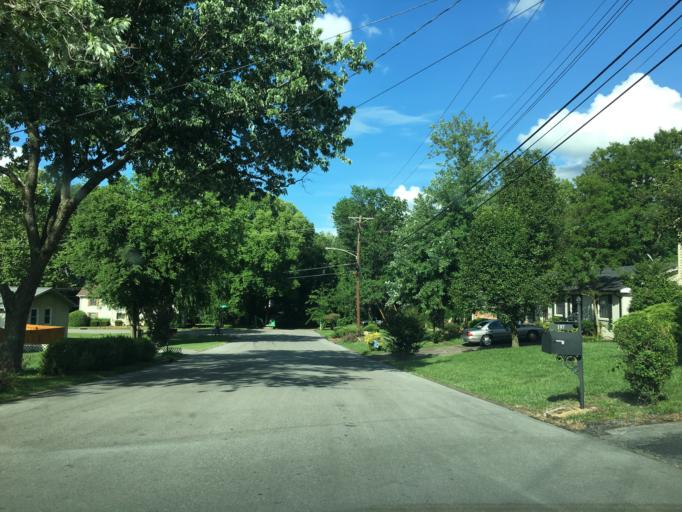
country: US
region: Tennessee
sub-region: Davidson County
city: Oak Hill
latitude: 36.0810
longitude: -86.7177
